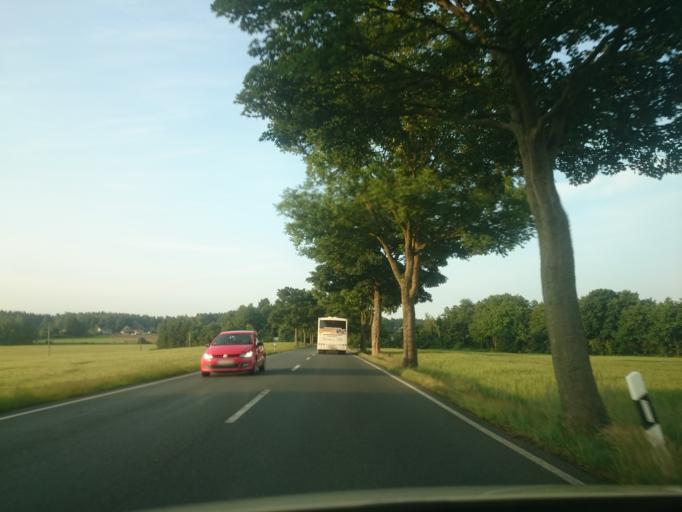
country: DE
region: Saxony
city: Brand-Erbisdorf
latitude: 50.8521
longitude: 13.3208
